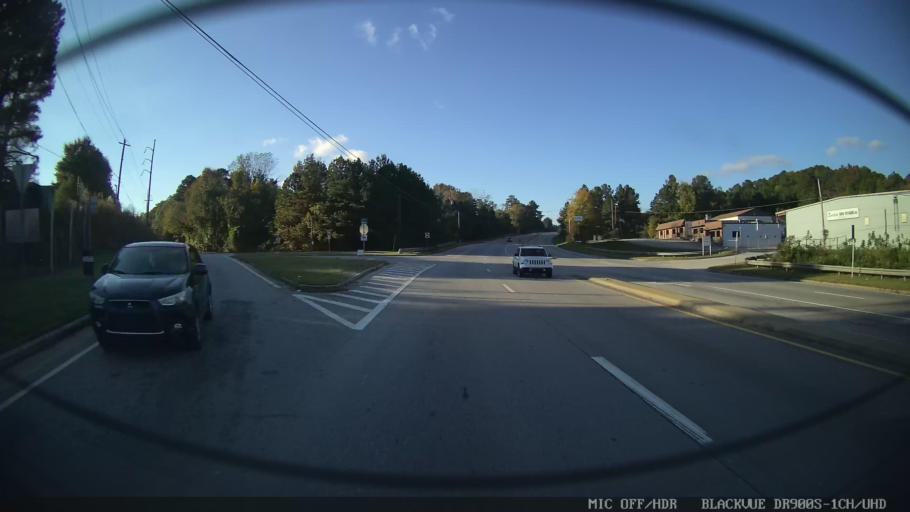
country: US
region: Georgia
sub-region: Clayton County
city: Conley
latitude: 33.6483
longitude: -84.3303
